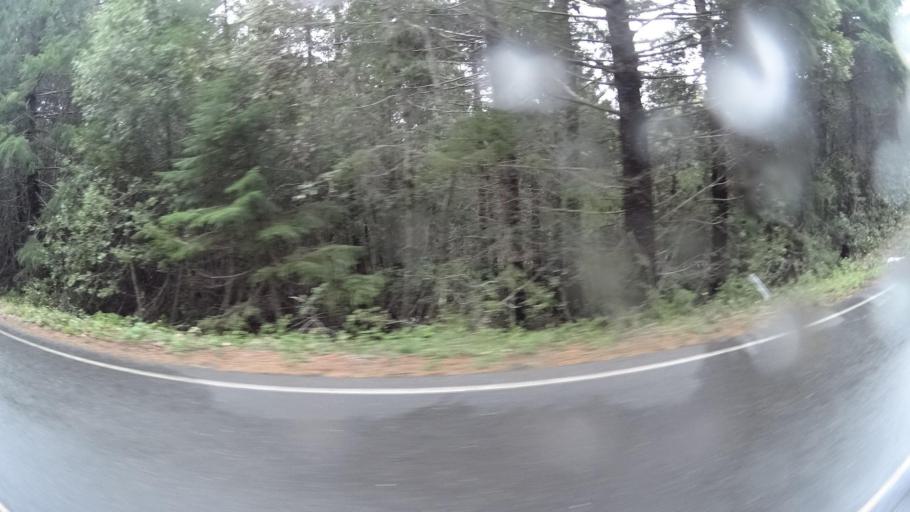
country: US
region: California
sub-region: Humboldt County
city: Willow Creek
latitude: 41.1679
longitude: -123.8153
